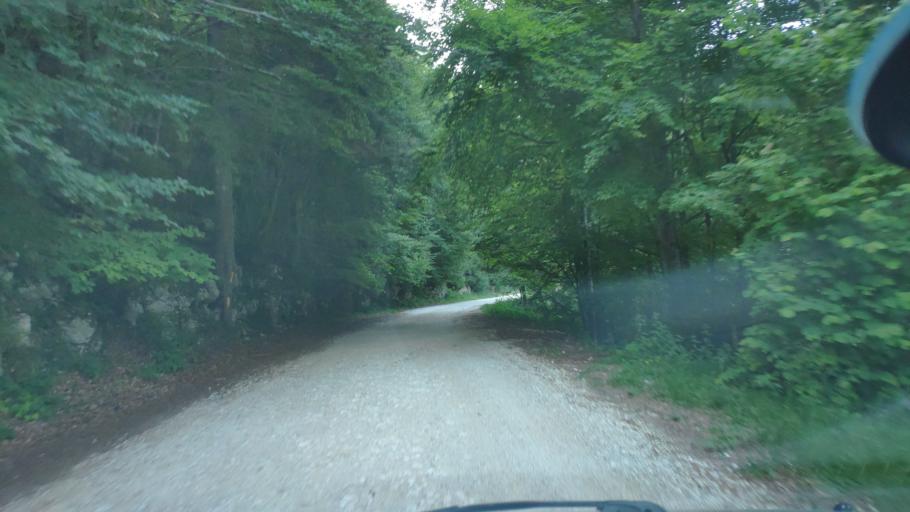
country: IT
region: Veneto
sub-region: Provincia di Vicenza
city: Calvene
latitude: 45.8008
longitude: 11.5006
